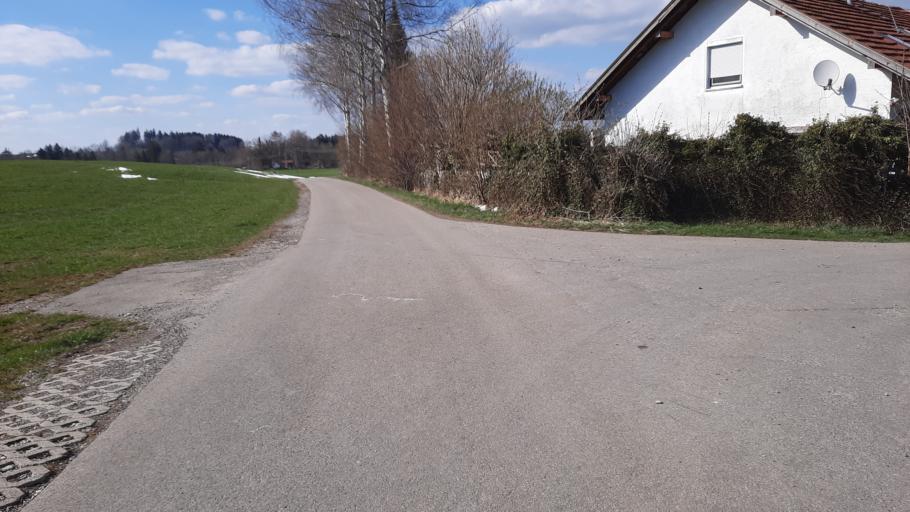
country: DE
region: Bavaria
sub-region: Swabia
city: Altusried
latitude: 47.8193
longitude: 10.2026
